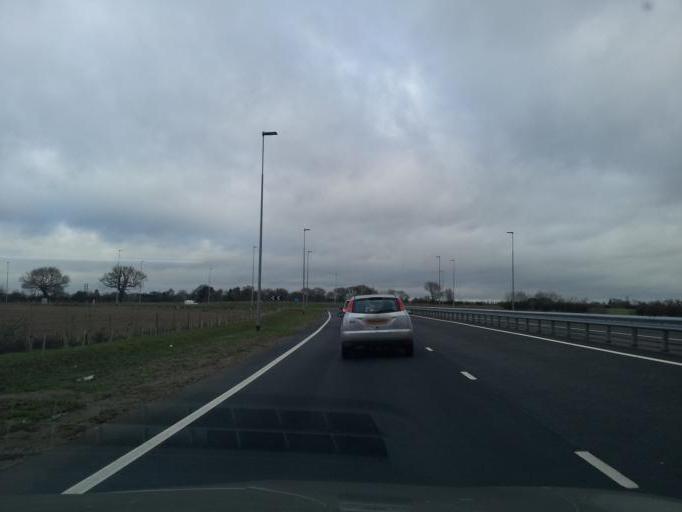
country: GB
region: England
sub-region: Norfolk
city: Surlingham
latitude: 52.6303
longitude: 1.3866
